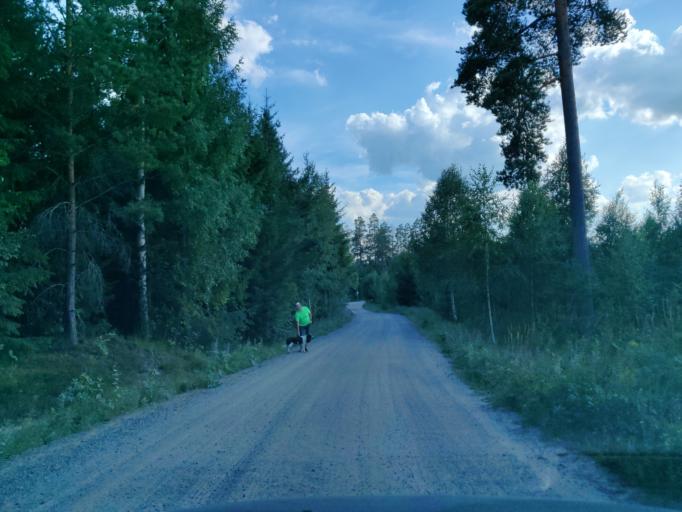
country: SE
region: Vaermland
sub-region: Hagfors Kommun
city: Hagfors
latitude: 60.0160
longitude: 13.6750
